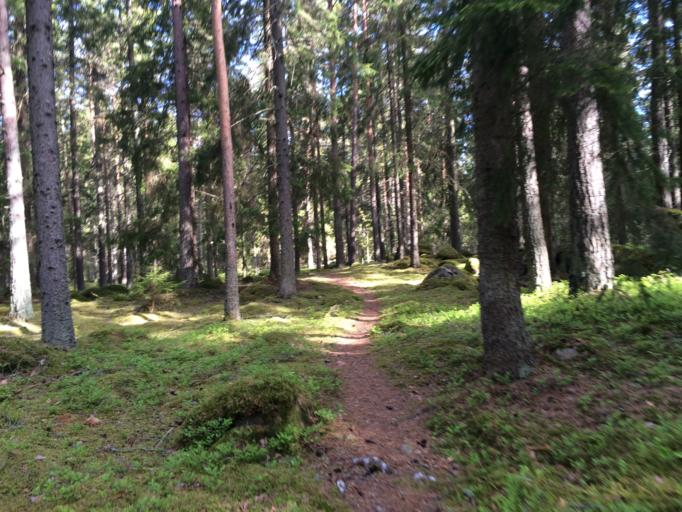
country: SE
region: Vaestmanland
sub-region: Hallstahammars Kommun
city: Hallstahammar
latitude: 59.6105
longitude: 16.2642
